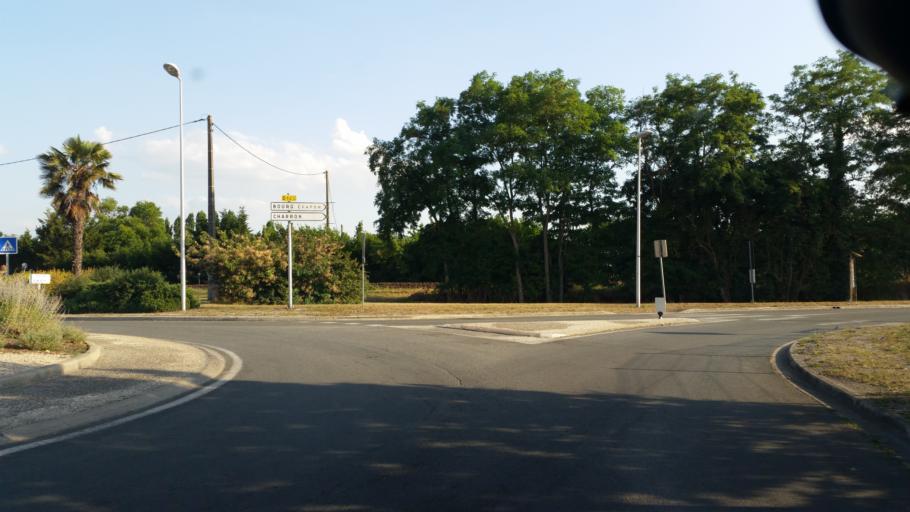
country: FR
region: Poitou-Charentes
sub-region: Departement de la Charente-Maritime
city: Marans
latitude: 46.3062
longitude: -1.0060
